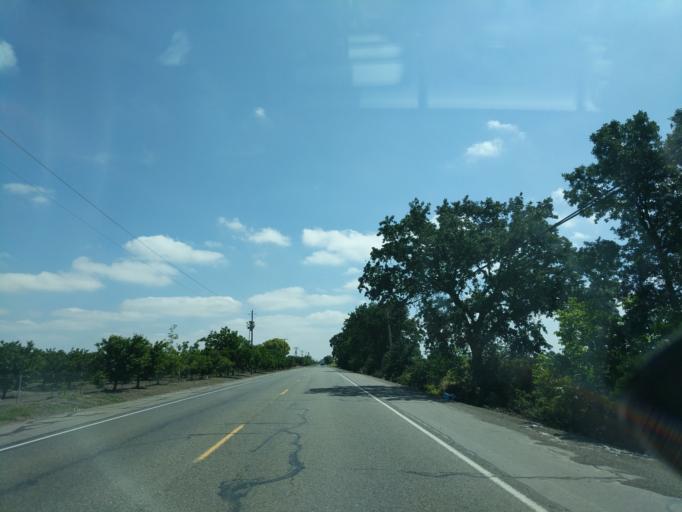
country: US
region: California
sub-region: San Joaquin County
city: Garden Acres
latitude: 37.9470
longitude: -121.2094
